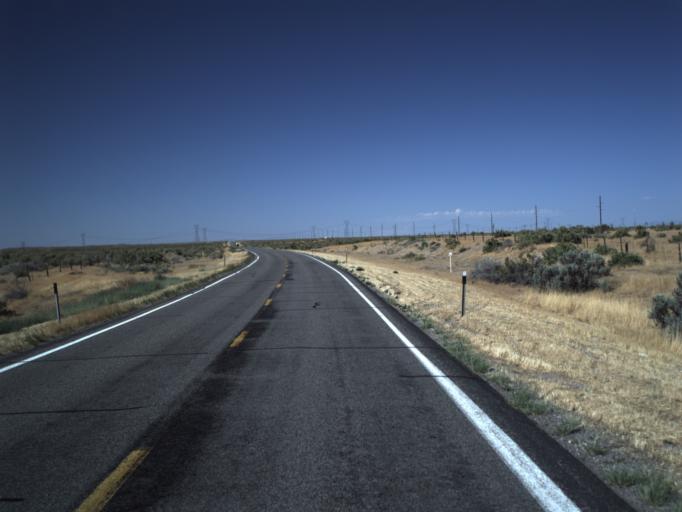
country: US
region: Utah
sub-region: Millard County
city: Delta
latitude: 39.5064
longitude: -112.3856
